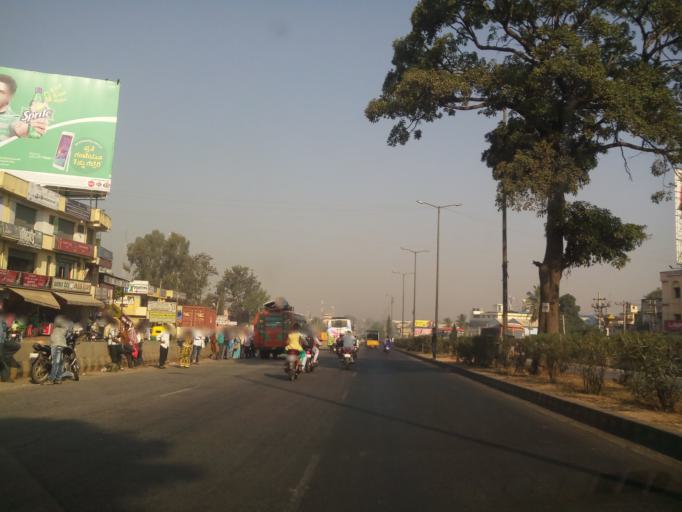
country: IN
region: Karnataka
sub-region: Bangalore Rural
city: Nelamangala
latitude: 13.0608
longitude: 77.4617
